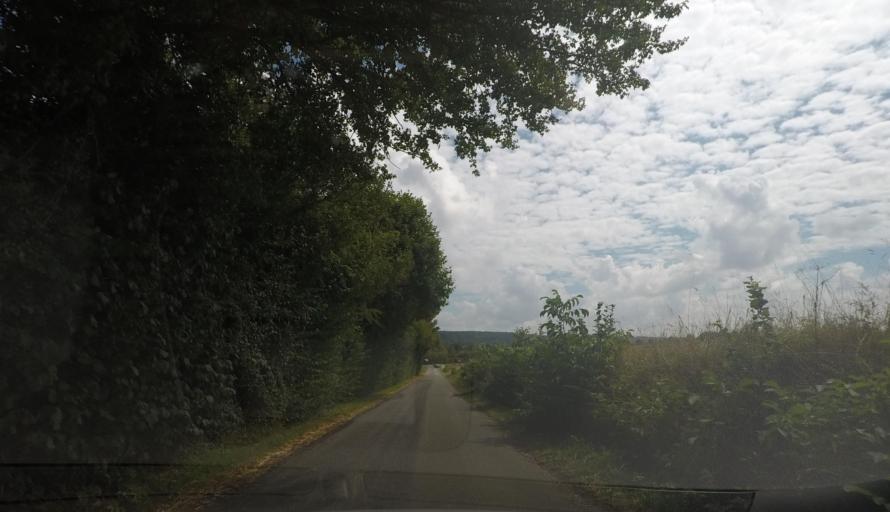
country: FR
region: Pays de la Loire
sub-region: Departement de la Sarthe
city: La Ferte-Bernard
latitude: 48.2654
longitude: 0.5976
